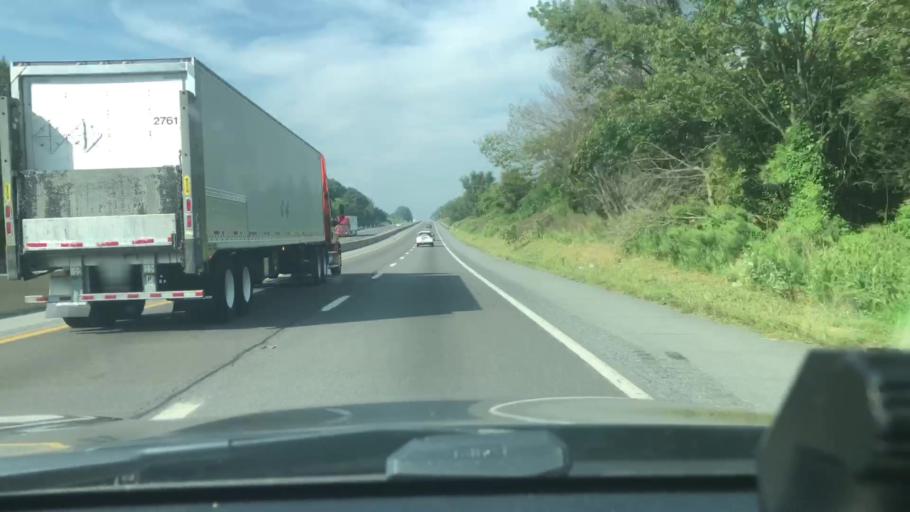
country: US
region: Pennsylvania
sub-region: Berks County
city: West Hamburg
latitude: 40.5428
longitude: -76.0342
